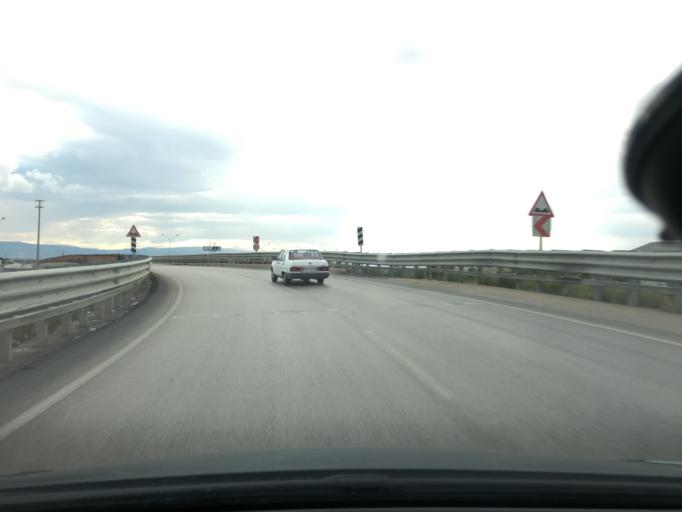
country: TR
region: Afyonkarahisar
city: Sincanli
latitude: 38.7972
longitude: 30.3907
